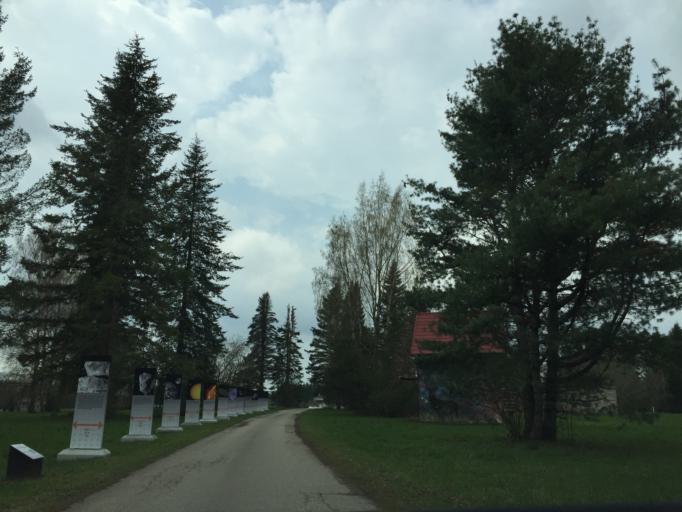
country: EE
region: Tartu
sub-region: Elva linn
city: Elva
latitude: 58.2653
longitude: 26.4654
